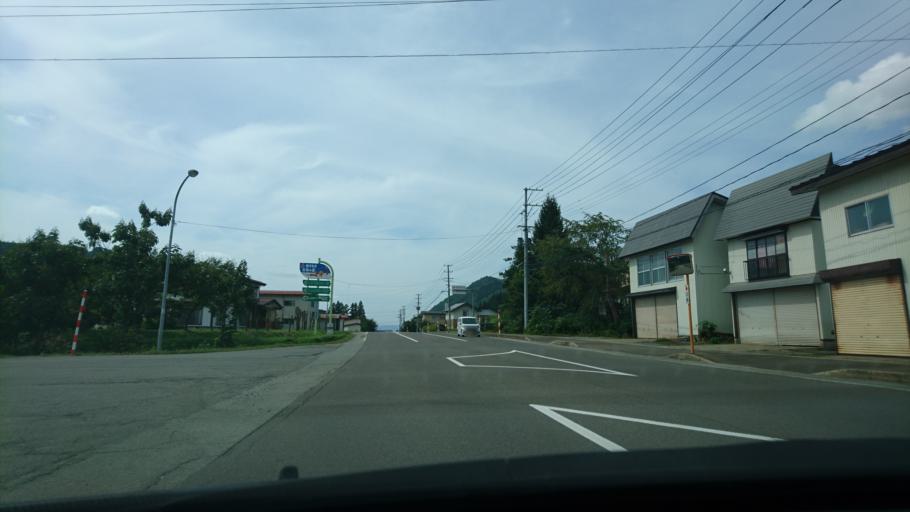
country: JP
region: Akita
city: Yuzawa
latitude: 39.1983
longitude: 140.6072
